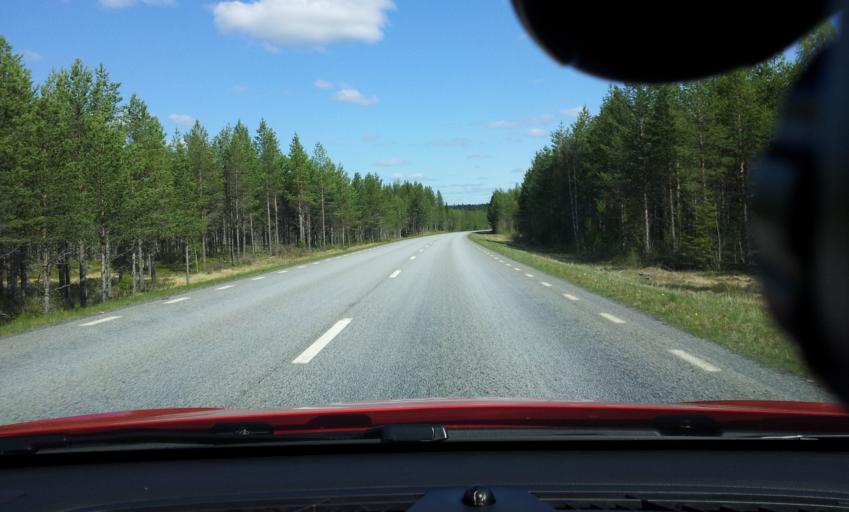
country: SE
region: Jaemtland
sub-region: Krokoms Kommun
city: Valla
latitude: 63.2824
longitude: 13.9316
